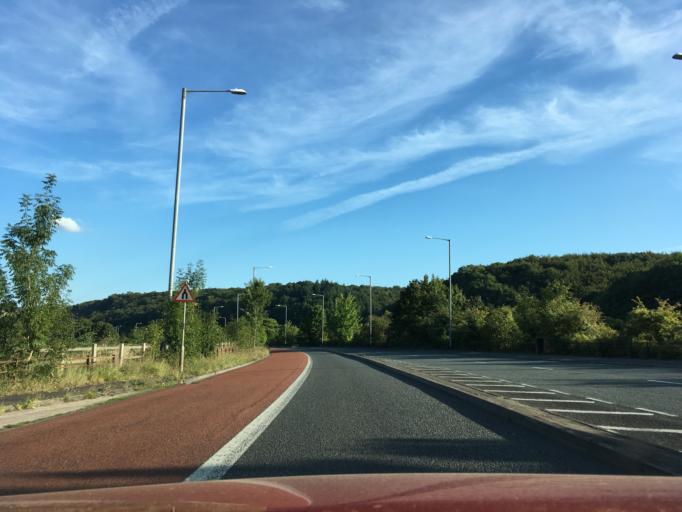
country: GB
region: England
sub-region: North Somerset
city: Long Ashton
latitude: 51.4749
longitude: -2.6485
